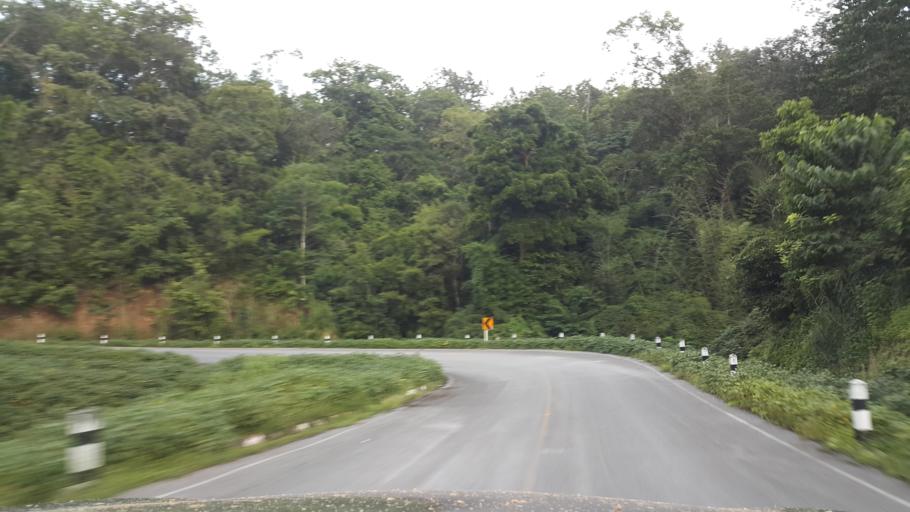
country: TH
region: Mae Hong Son
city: Mae Hi
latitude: 19.2456
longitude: 98.4594
